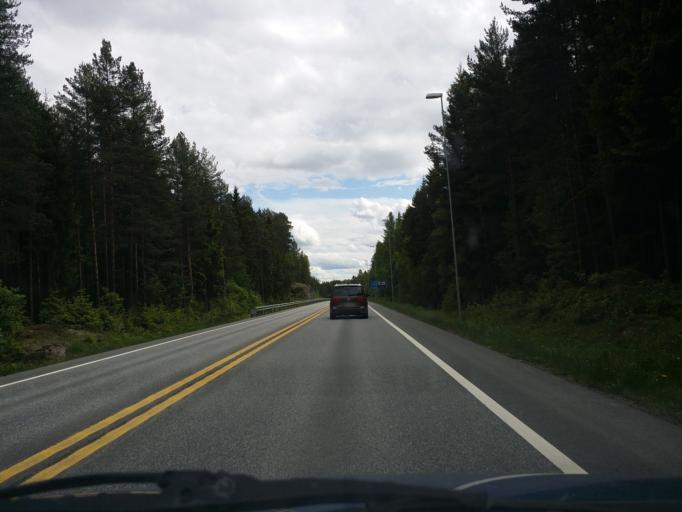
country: NO
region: Hedmark
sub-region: Stange
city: Stange
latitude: 60.7146
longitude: 11.2475
